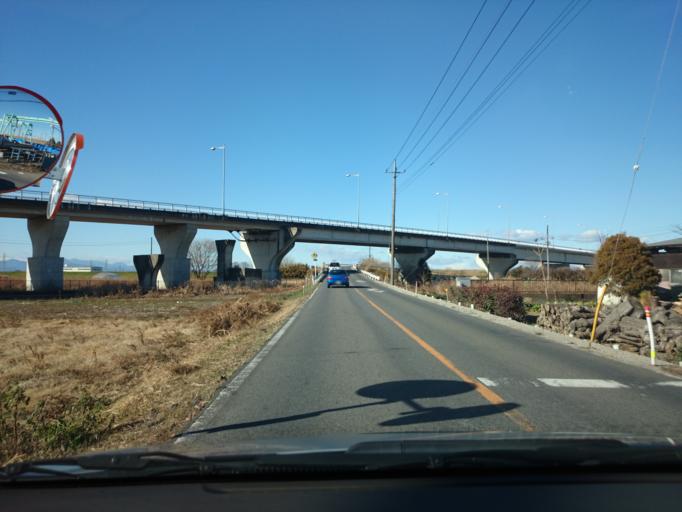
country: JP
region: Saitama
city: Fukayacho
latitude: 36.2295
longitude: 139.3119
